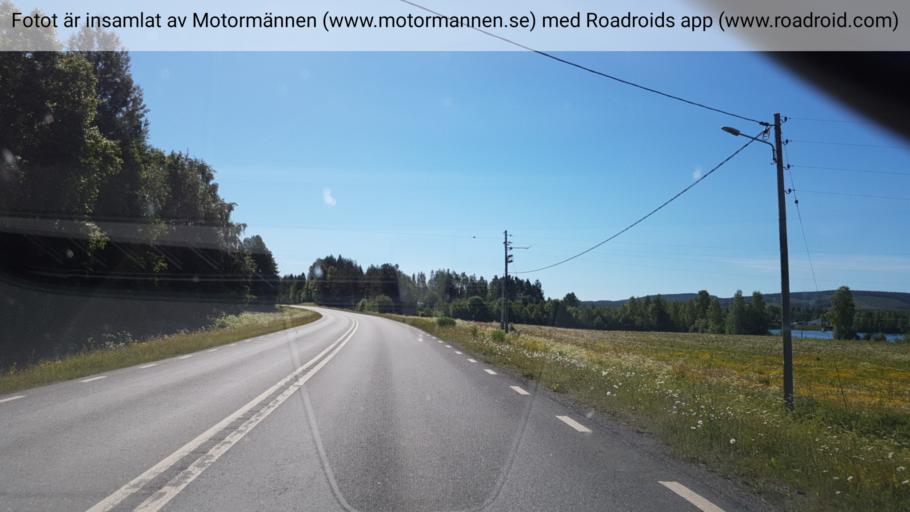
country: SE
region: Norrbotten
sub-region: Bodens Kommun
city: Boden
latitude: 65.8646
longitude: 21.4198
